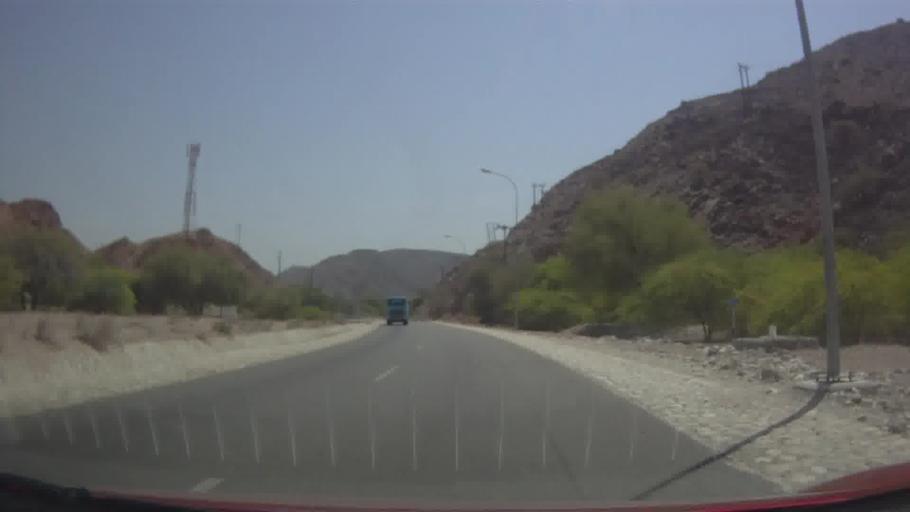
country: OM
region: Muhafazat Masqat
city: Muscat
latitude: 23.5084
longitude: 58.6503
